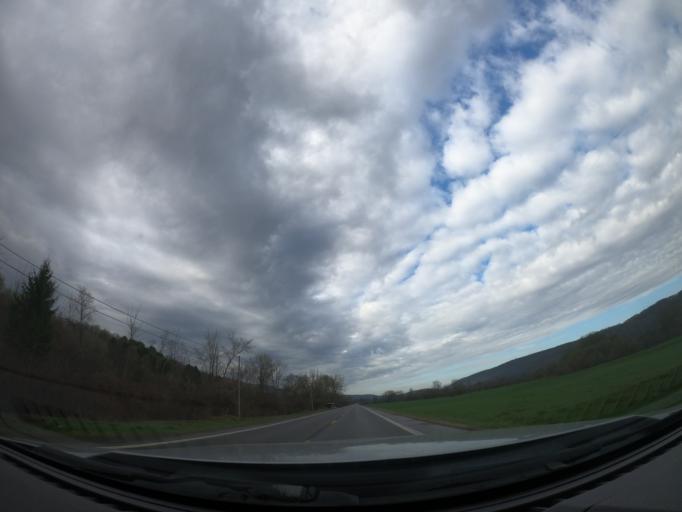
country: US
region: New York
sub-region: Cortland County
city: McGraw
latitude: 42.7331
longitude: -75.9554
